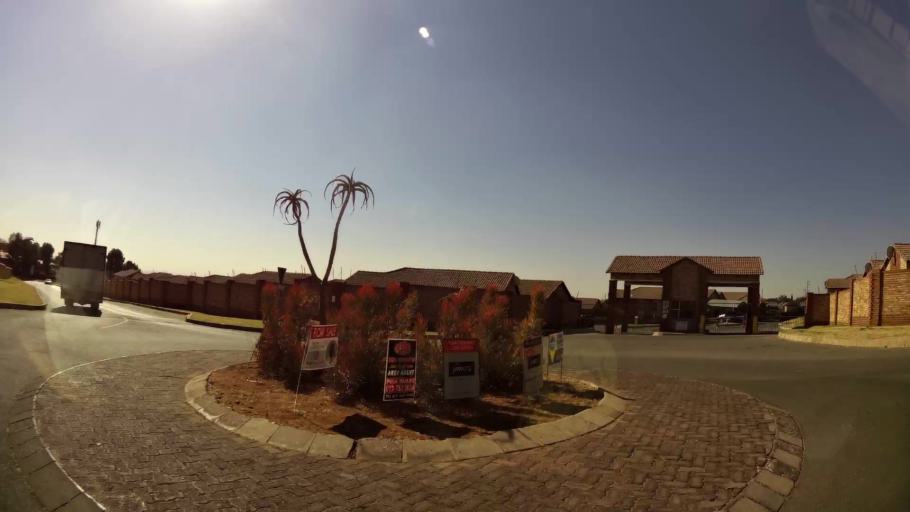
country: ZA
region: Gauteng
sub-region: City of Johannesburg Metropolitan Municipality
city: Modderfontein
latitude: -26.0737
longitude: 28.1945
